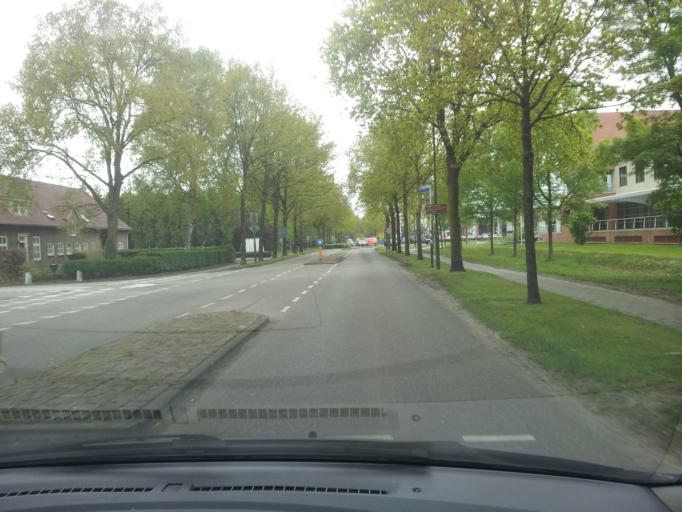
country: NL
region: North Brabant
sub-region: Gemeente Bernheze
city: Heesch
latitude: 51.7322
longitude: 5.5113
